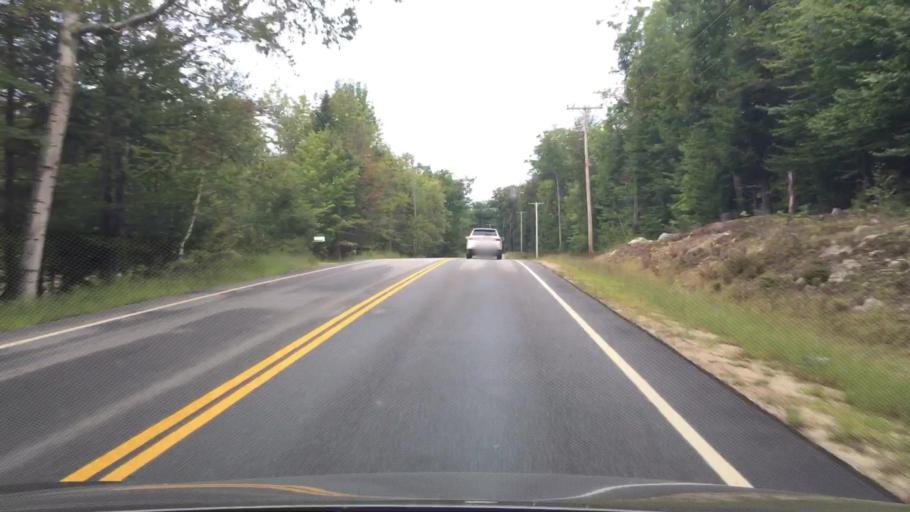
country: US
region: Maine
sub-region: Oxford County
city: Hartford
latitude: 44.3592
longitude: -70.3090
